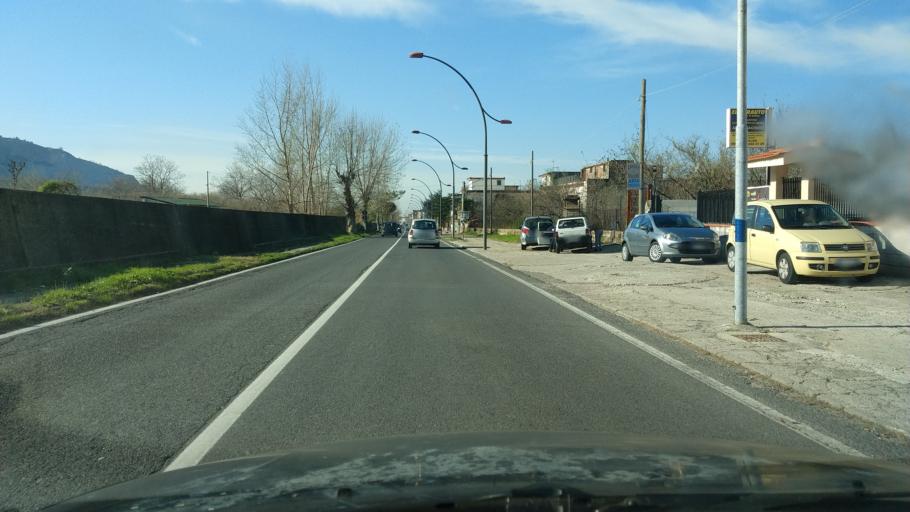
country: IT
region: Campania
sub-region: Provincia di Napoli
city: Tufino
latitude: 40.9490
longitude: 14.5816
